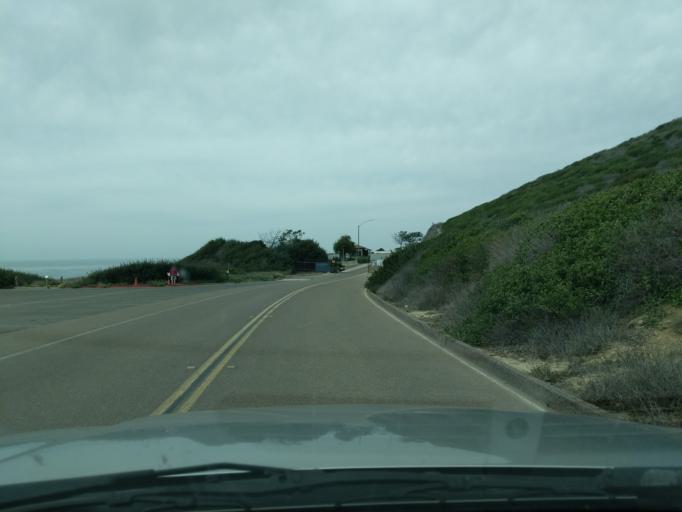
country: US
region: California
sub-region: San Diego County
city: Coronado
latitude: 32.6749
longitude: -117.2456
